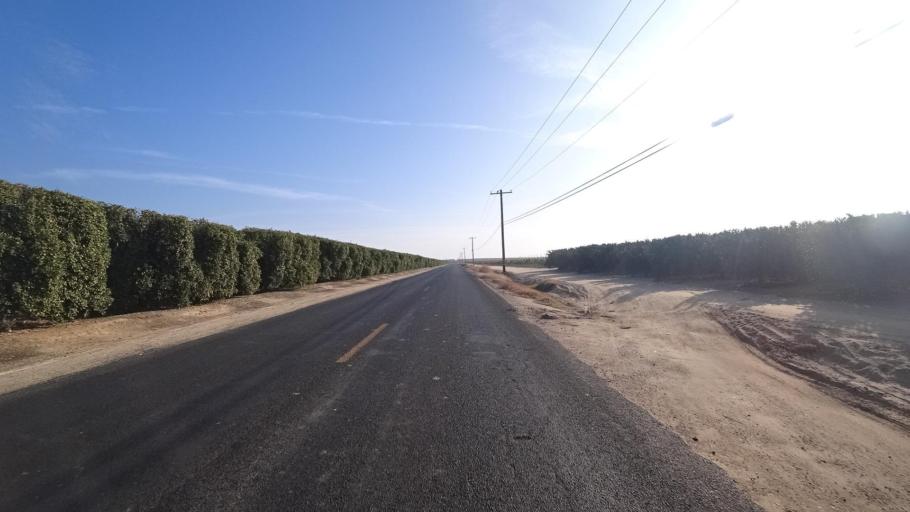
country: US
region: California
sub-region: Kern County
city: McFarland
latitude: 35.6746
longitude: -119.1468
